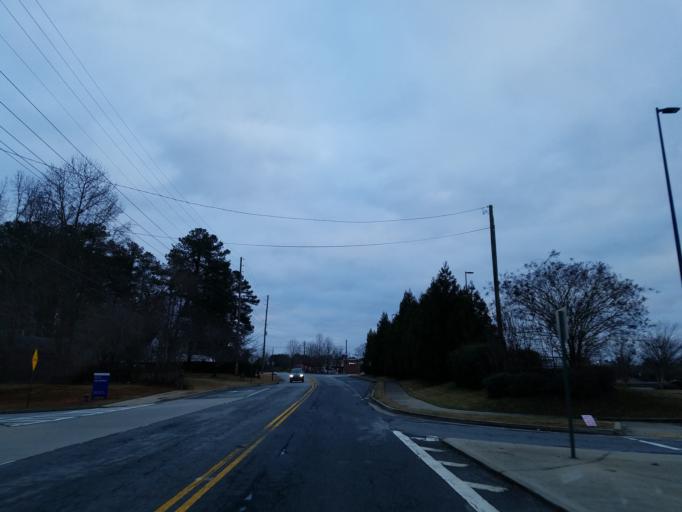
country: US
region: Georgia
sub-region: Cobb County
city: Acworth
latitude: 34.0471
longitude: -84.6961
